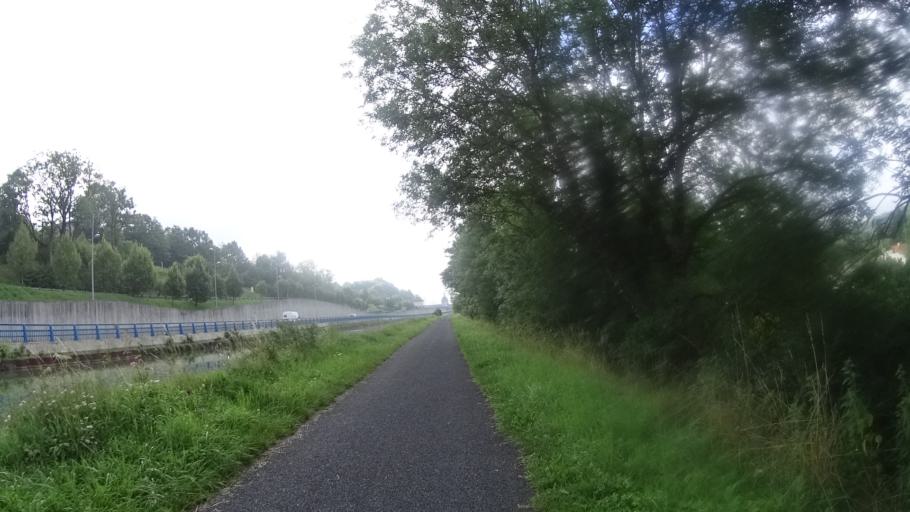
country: FR
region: Lorraine
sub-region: Departement de la Meuse
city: Bar-le-Duc
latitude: 48.7852
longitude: 5.1519
